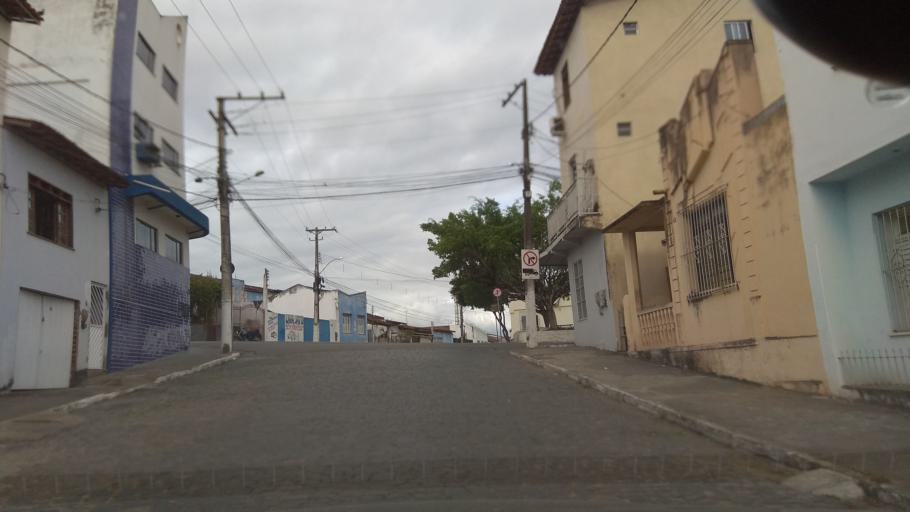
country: BR
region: Bahia
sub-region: Ipiau
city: Ipiau
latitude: -14.1372
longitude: -39.7374
